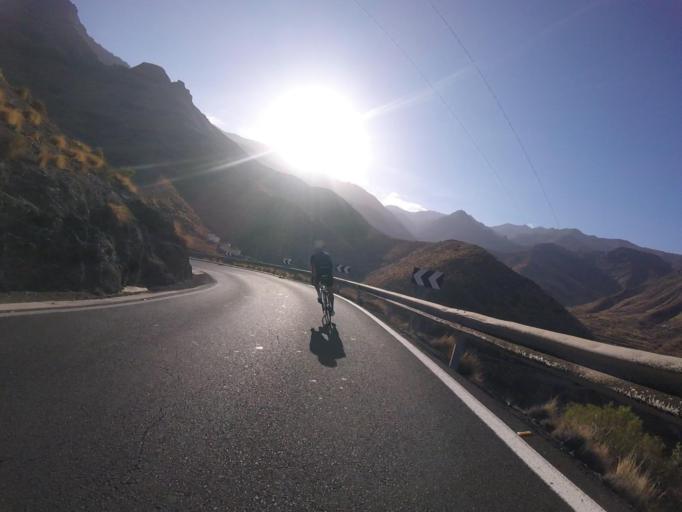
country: ES
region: Canary Islands
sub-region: Provincia de Las Palmas
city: Agaete
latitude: 28.0528
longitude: -15.7329
